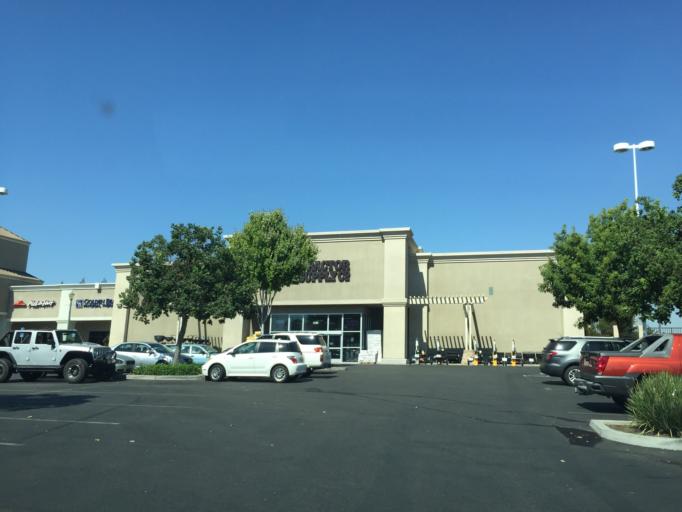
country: US
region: California
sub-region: Stanislaus County
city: Oakdale
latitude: 37.7741
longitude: -120.8292
